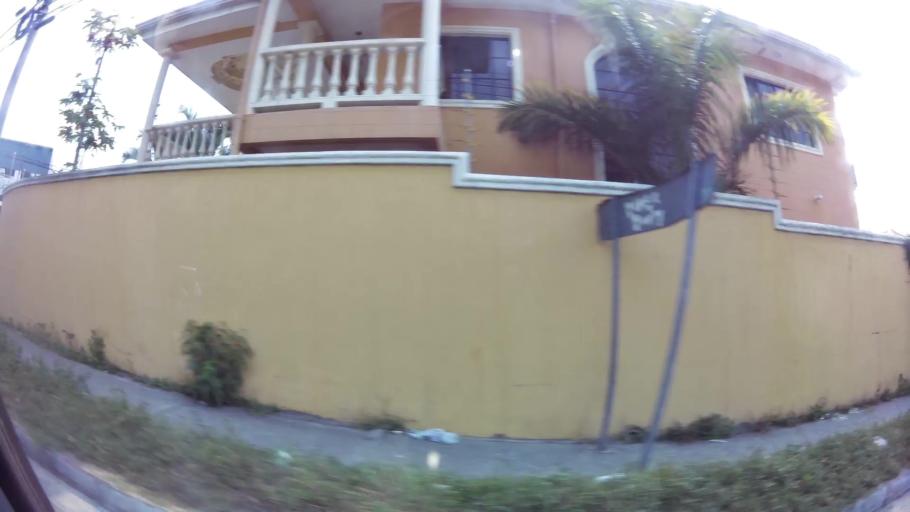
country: HN
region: Cortes
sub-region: San Pedro Sula
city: Pena Blanca
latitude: 15.5489
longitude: -88.0358
